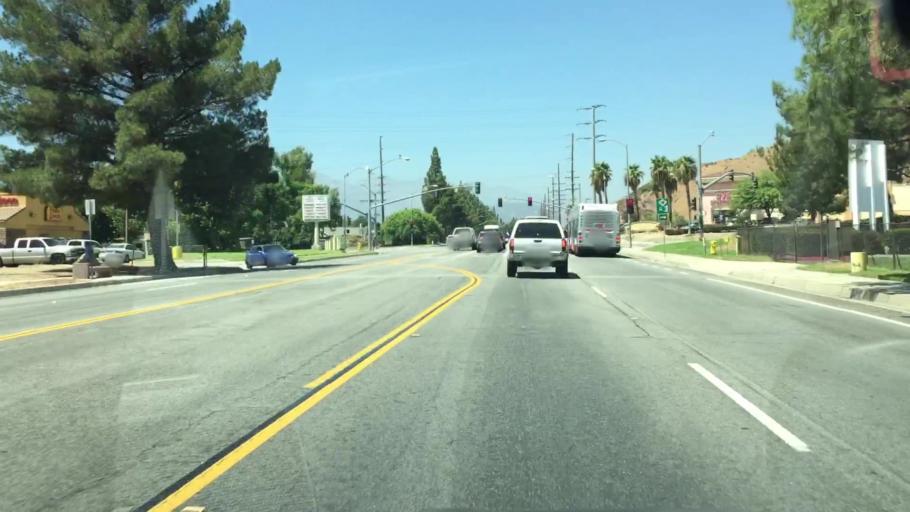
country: US
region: California
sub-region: San Bernardino County
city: Muscoy
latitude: 34.1757
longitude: -117.3299
